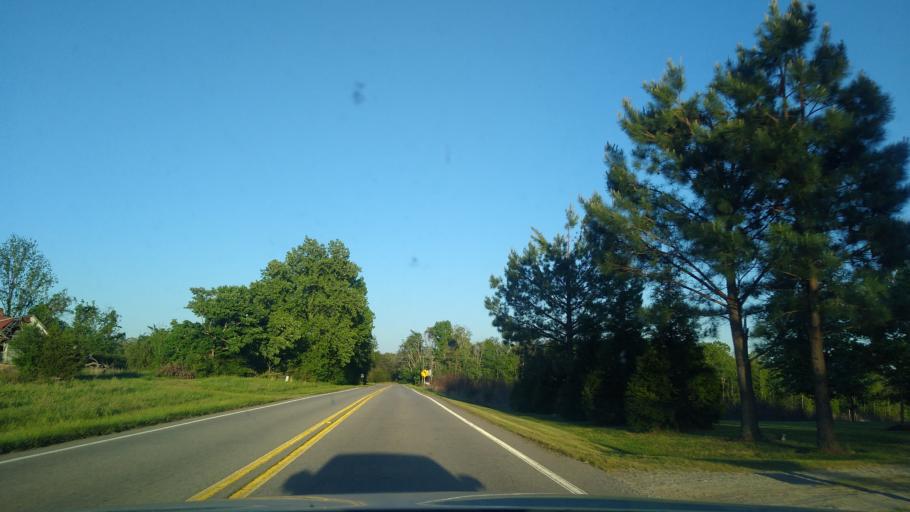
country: US
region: North Carolina
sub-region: Rockingham County
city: Reidsville
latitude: 36.3786
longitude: -79.5877
